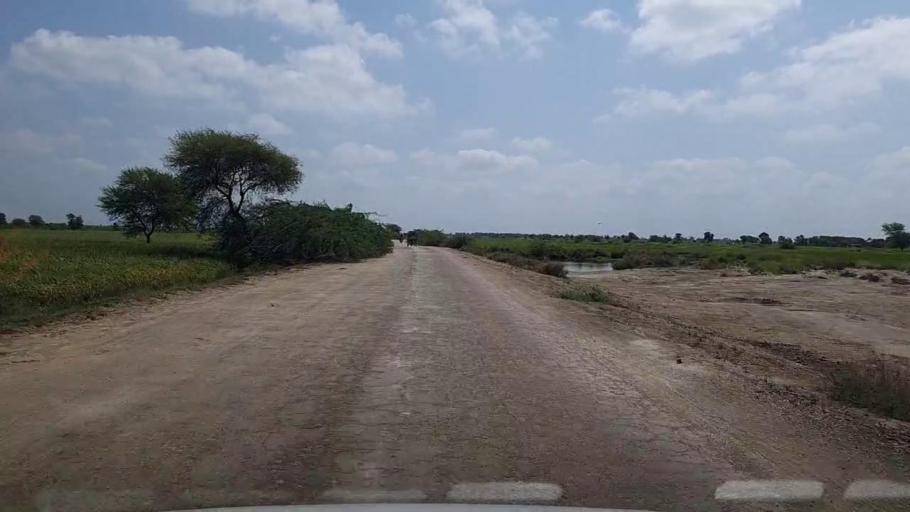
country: PK
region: Sindh
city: Talhar
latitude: 24.8866
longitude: 68.7040
